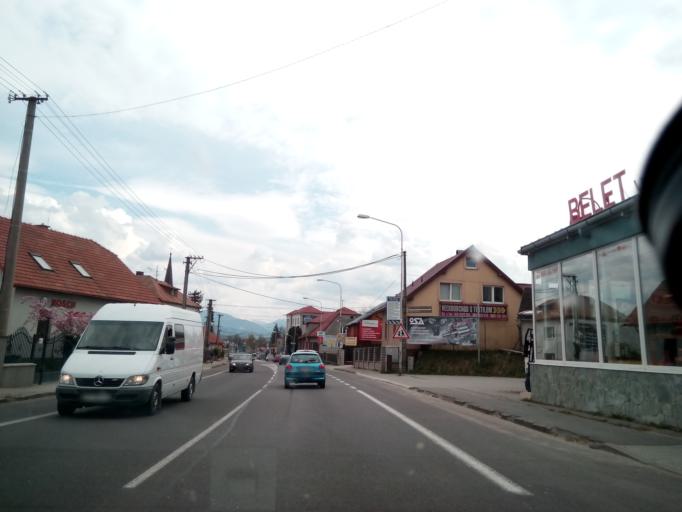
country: SK
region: Zilinsky
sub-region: Okres Zilina
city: Vrutky
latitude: 49.1167
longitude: 18.9130
